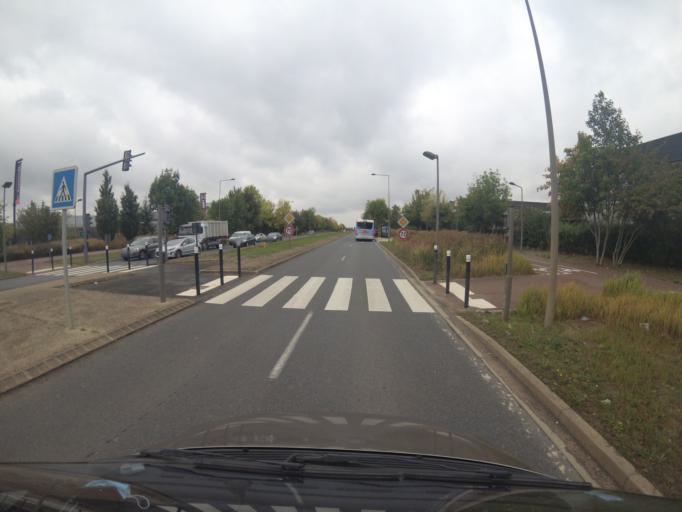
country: FR
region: Ile-de-France
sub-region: Departement de Seine-et-Marne
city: Chanteloup-en-Brie
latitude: 48.8546
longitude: 2.7587
